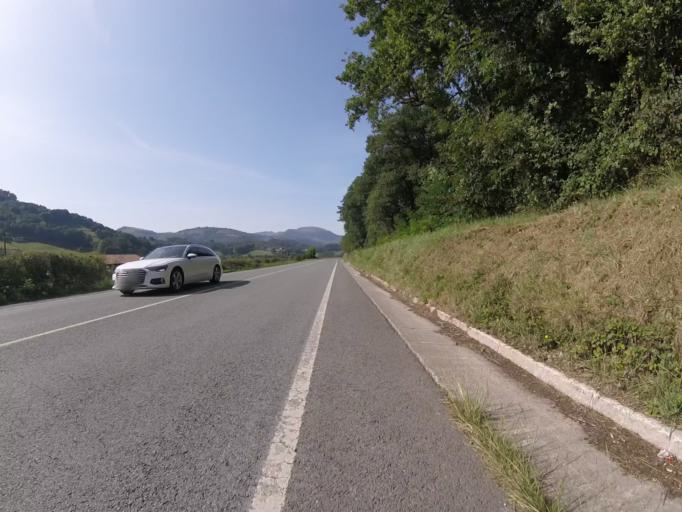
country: ES
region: Navarre
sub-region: Provincia de Navarra
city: Zugarramurdi
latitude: 43.1536
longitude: -1.5039
